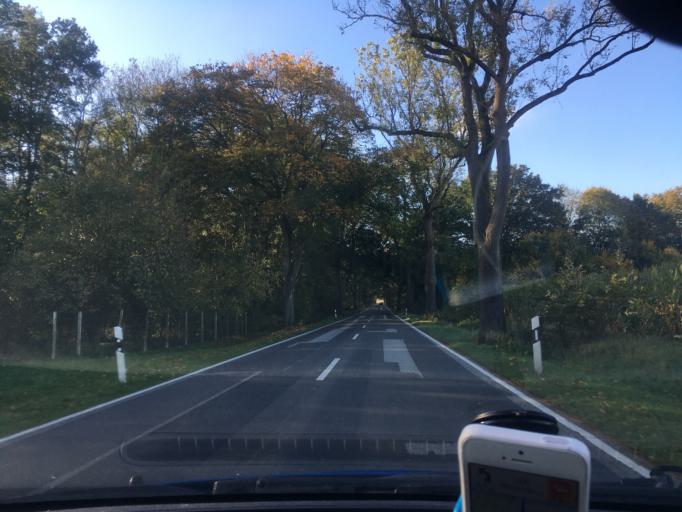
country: DE
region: Mecklenburg-Vorpommern
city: Zarrentin
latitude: 53.5266
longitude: 10.9776
